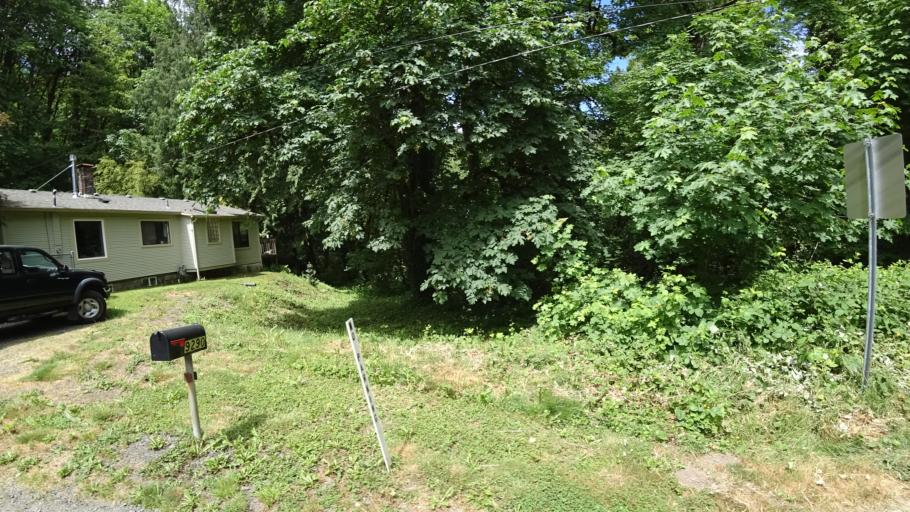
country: US
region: Oregon
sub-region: Washington County
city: West Haven
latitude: 45.5852
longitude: -122.7771
